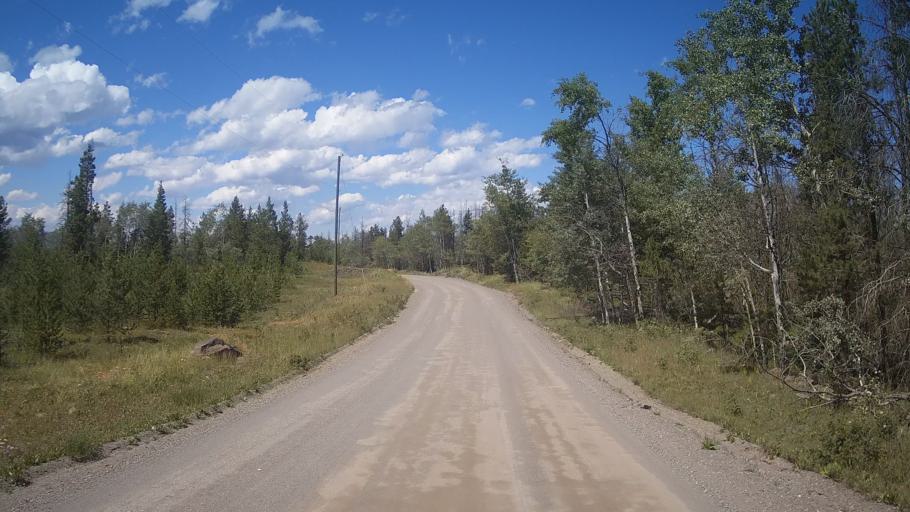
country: CA
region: British Columbia
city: Cache Creek
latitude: 51.2487
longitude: -121.6635
